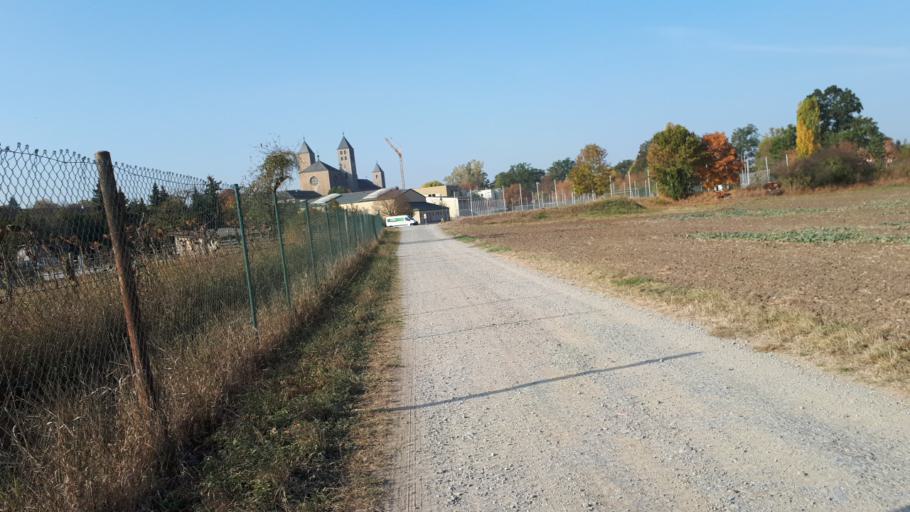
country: DE
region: Bavaria
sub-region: Regierungsbezirk Unterfranken
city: Sommerach
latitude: 49.8068
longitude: 10.2371
